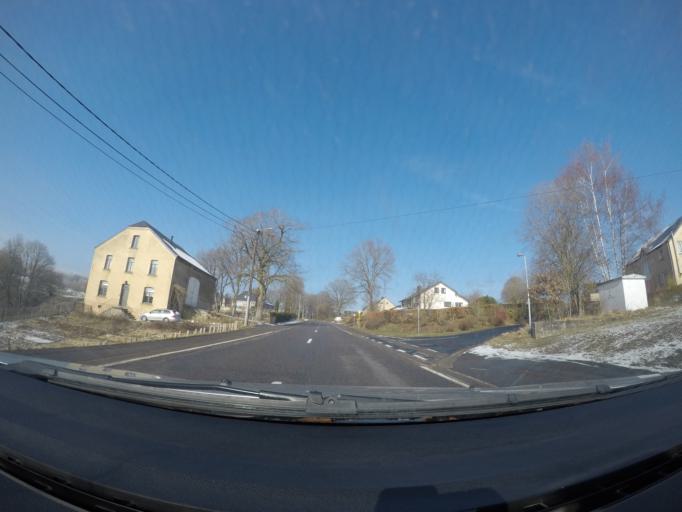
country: BE
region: Wallonia
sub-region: Province du Luxembourg
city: Tintigny
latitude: 49.7291
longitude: 5.5325
